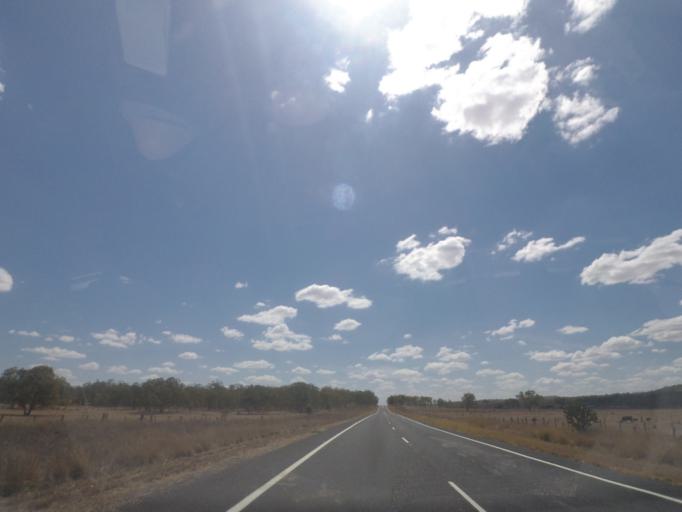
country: AU
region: Queensland
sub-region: Southern Downs
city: Warwick
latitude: -28.1838
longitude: 151.8123
